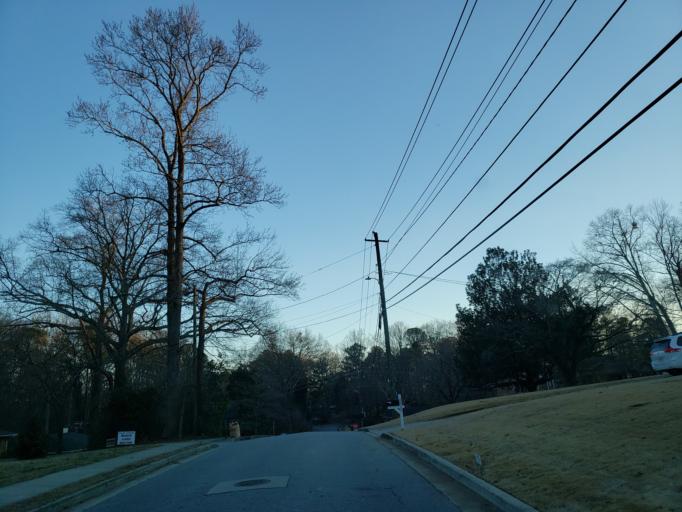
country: US
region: Georgia
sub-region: Cobb County
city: Smyrna
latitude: 33.8702
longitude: -84.5158
